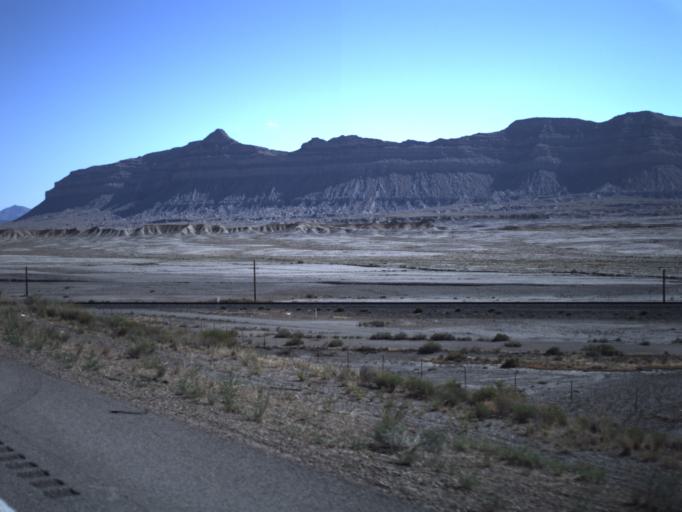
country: US
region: Utah
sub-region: Carbon County
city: East Carbon City
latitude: 39.1340
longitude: -110.3377
